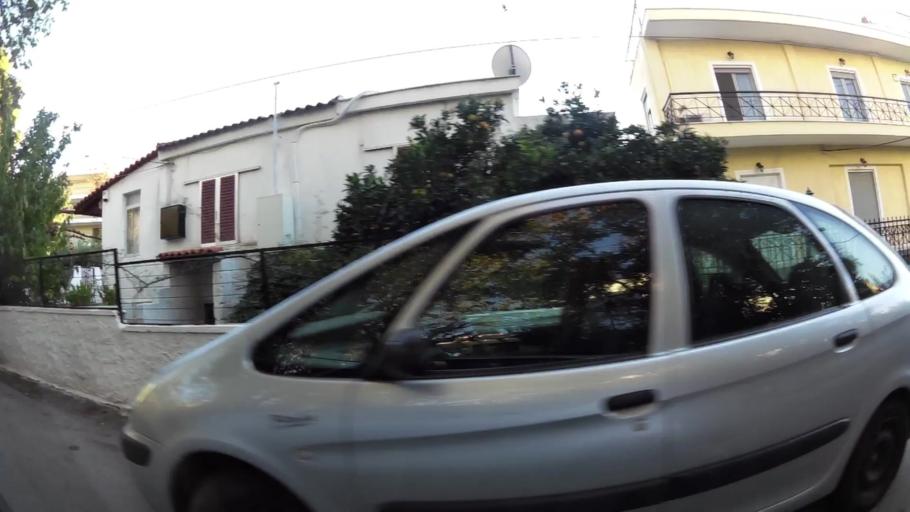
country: GR
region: Attica
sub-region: Nomarchia Athinas
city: Kifisia
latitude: 38.0702
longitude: 23.8015
